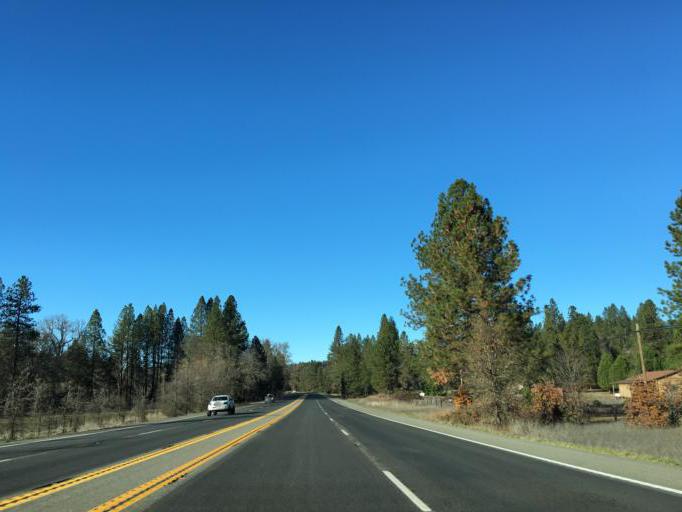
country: US
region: California
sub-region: Mendocino County
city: Laytonville
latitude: 39.7233
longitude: -123.5027
